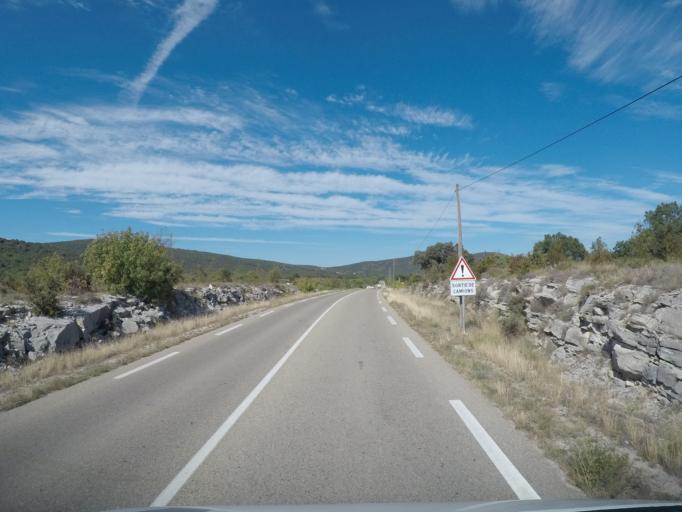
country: FR
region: Languedoc-Roussillon
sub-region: Departement de l'Herault
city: Saint-Martin-de-Londres
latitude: 43.8226
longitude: 3.7445
